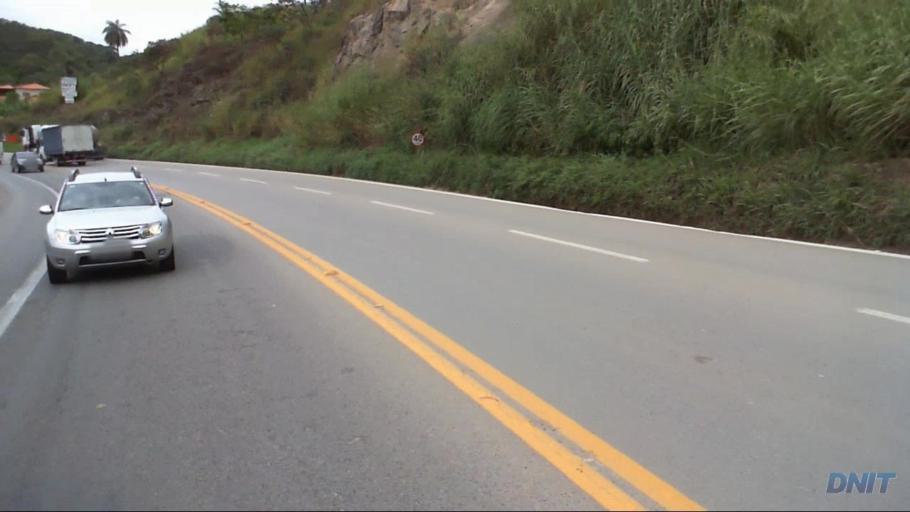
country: BR
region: Minas Gerais
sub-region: Caete
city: Caete
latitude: -19.7866
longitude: -43.6632
